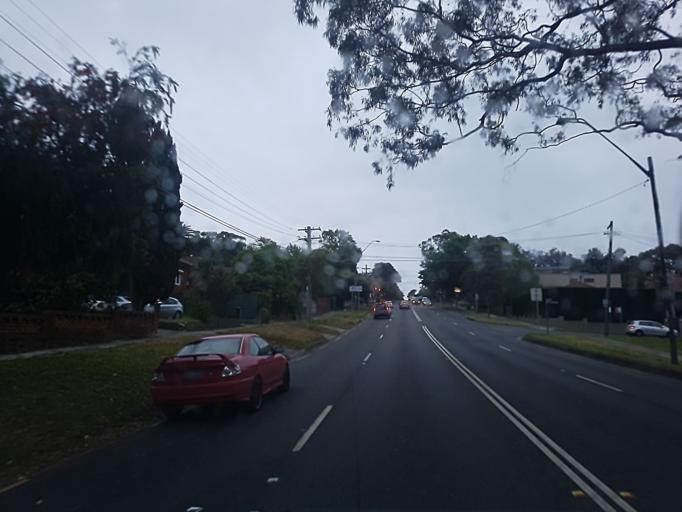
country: AU
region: New South Wales
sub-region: Willoughby
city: Castle Cove
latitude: -33.7986
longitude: 151.2099
